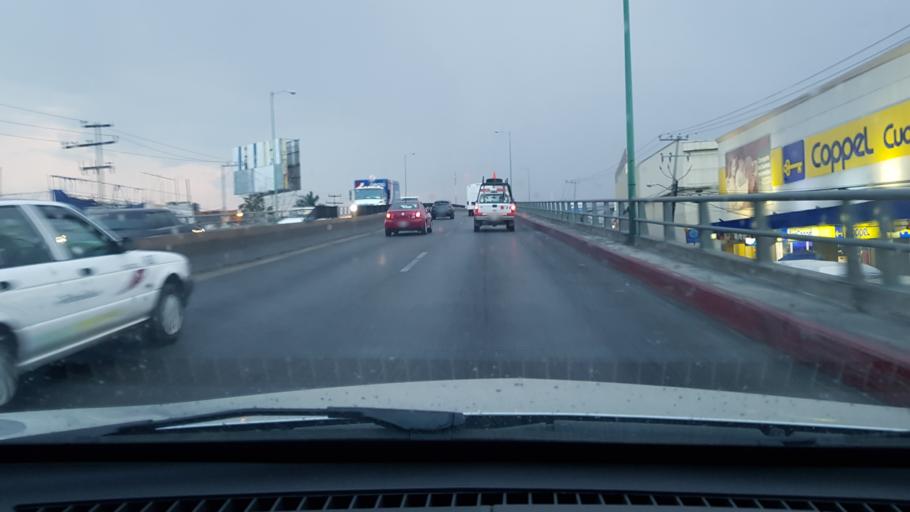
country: MX
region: Morelos
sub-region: Tepoztlan
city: Loma Bonita
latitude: 18.9198
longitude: -99.1965
